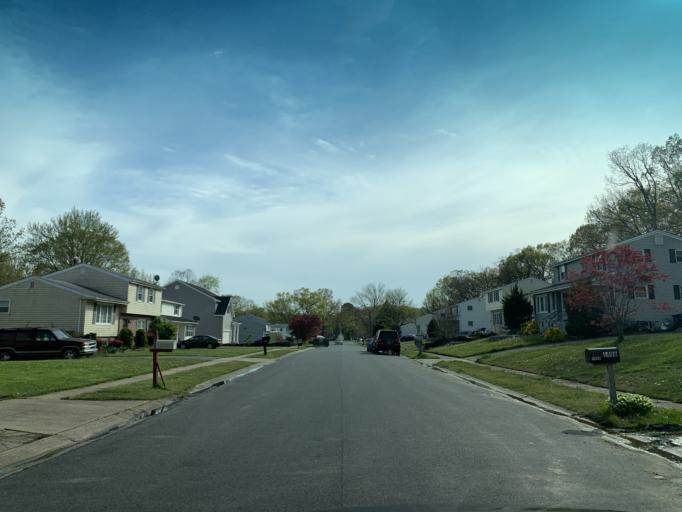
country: US
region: Maryland
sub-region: Harford County
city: Perryman
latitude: 39.4805
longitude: -76.2047
